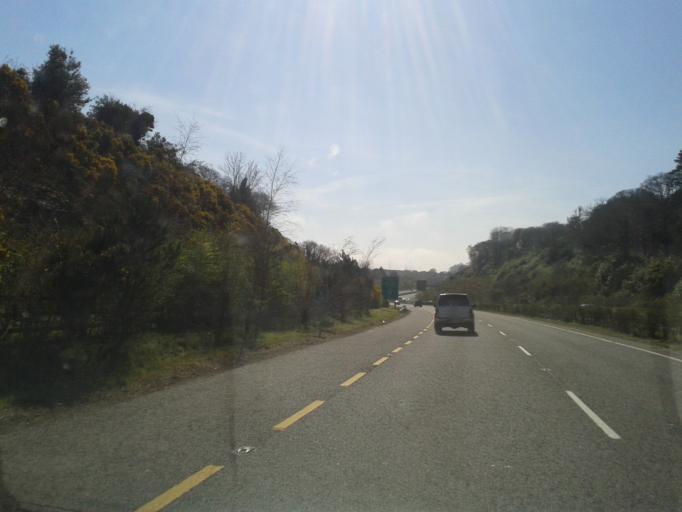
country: IE
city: Newtownmountkennedy
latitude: 53.0602
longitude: -6.0929
